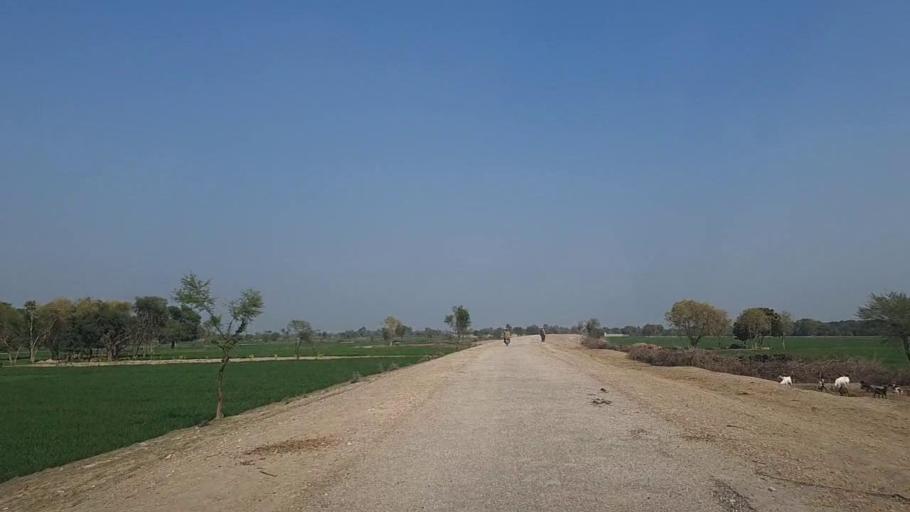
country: PK
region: Sindh
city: Moro
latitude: 26.7970
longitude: 67.9397
